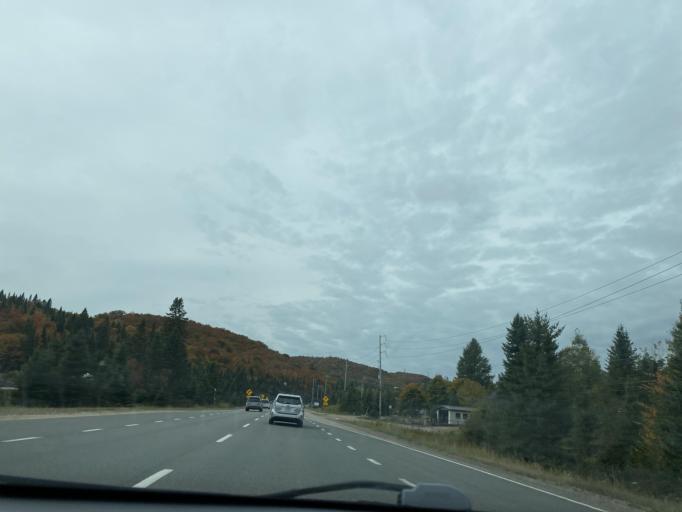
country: CA
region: Quebec
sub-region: Laurentides
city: Sainte-Agathe-des-Monts
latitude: 46.1041
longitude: -74.4067
